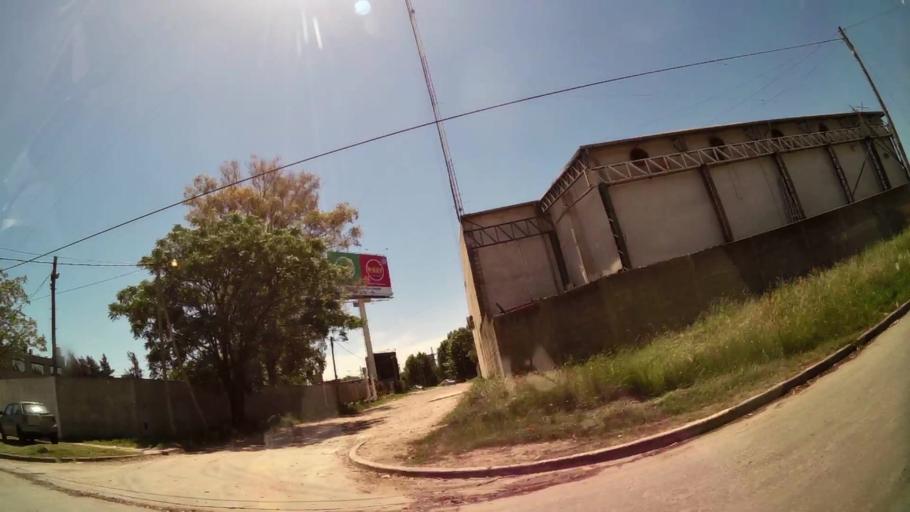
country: AR
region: Buenos Aires
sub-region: Partido de Tigre
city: Tigre
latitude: -34.4808
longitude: -58.6464
